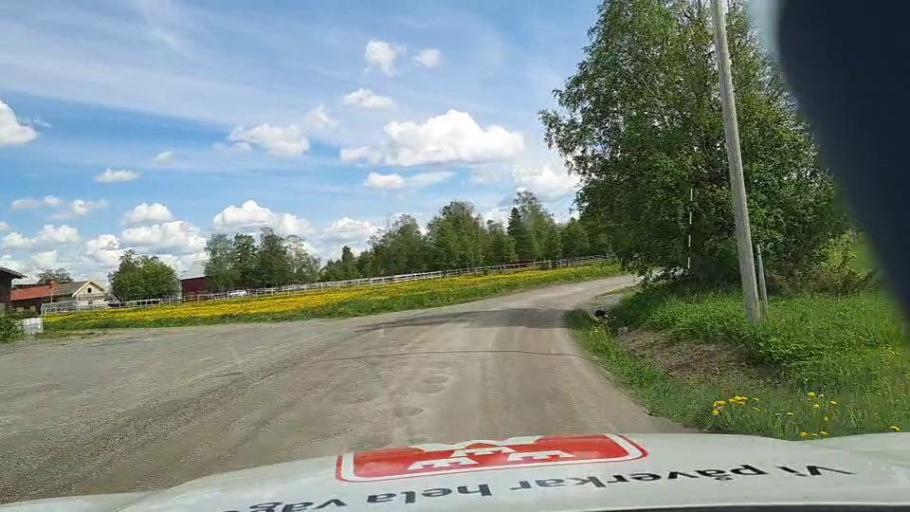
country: SE
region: Jaemtland
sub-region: OEstersunds Kommun
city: Brunflo
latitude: 63.0021
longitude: 14.8038
